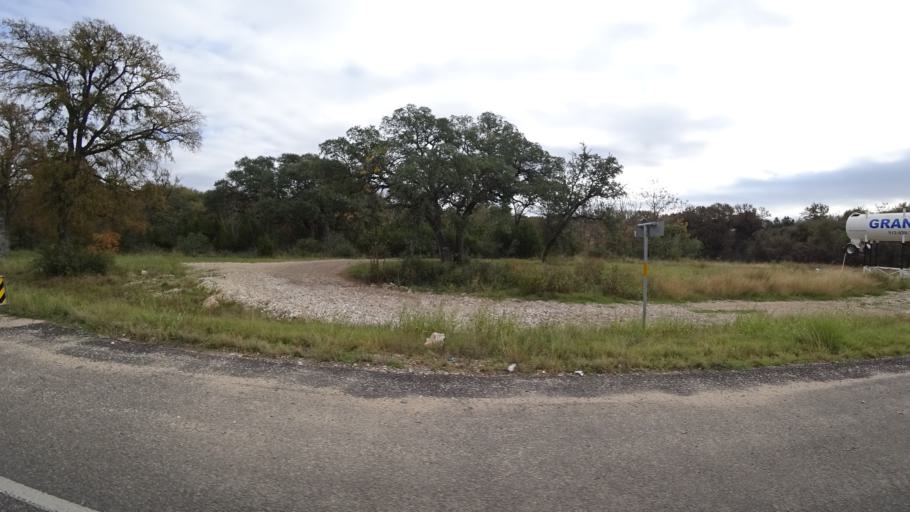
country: US
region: Texas
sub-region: Travis County
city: Manchaca
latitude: 30.1394
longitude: -97.8481
